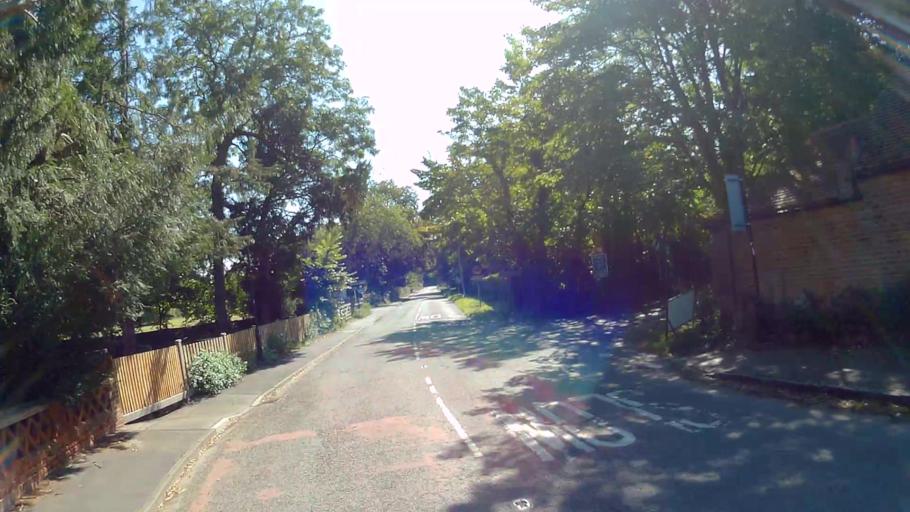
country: GB
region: England
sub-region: Wokingham
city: Swallowfield
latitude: 51.3792
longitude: -0.9561
